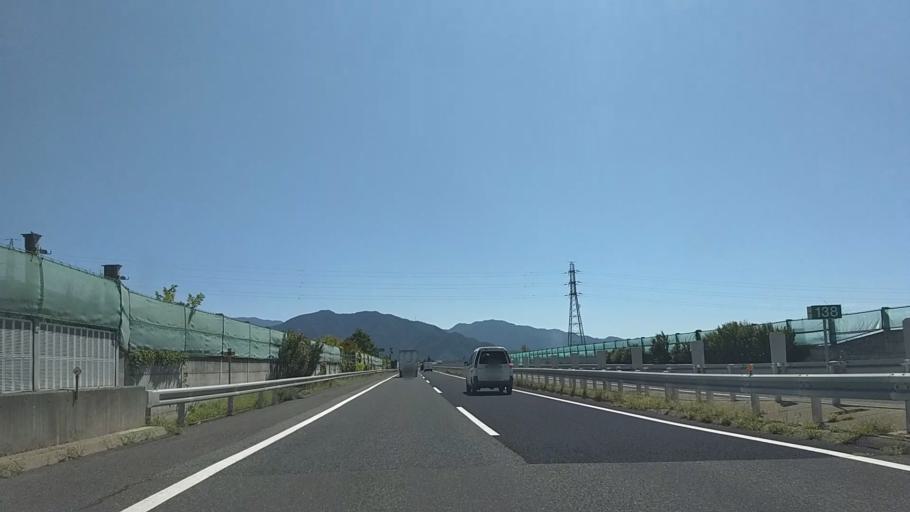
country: JP
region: Nagano
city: Suzaka
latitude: 36.6624
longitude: 138.2828
